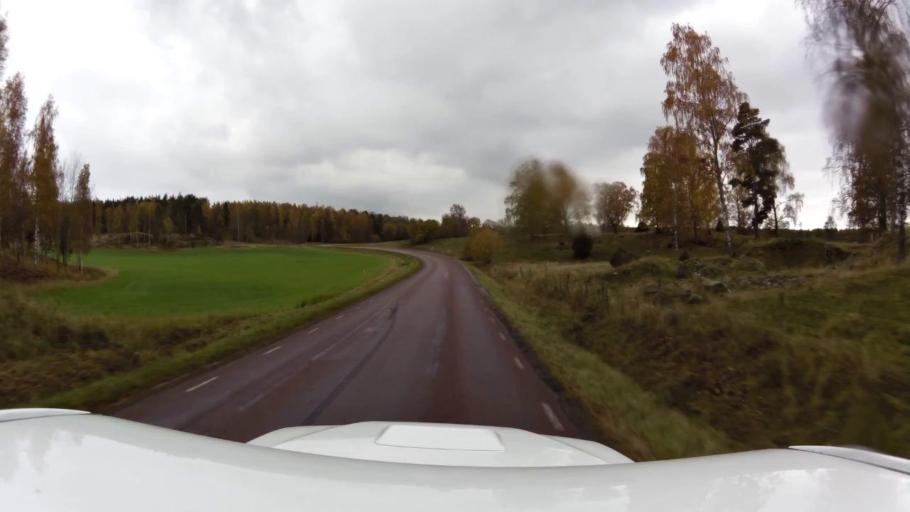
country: SE
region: OEstergoetland
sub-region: Linkopings Kommun
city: Ljungsbro
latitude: 58.5325
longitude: 15.5241
